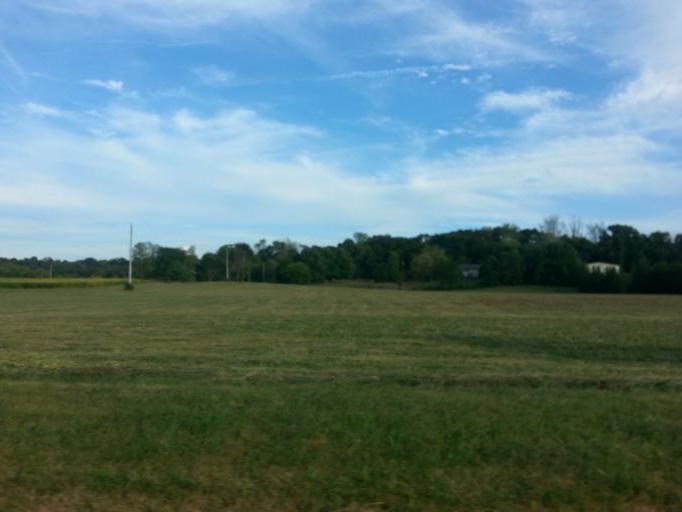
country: US
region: Tennessee
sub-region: Blount County
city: Wildwood
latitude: 35.8232
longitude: -83.8862
